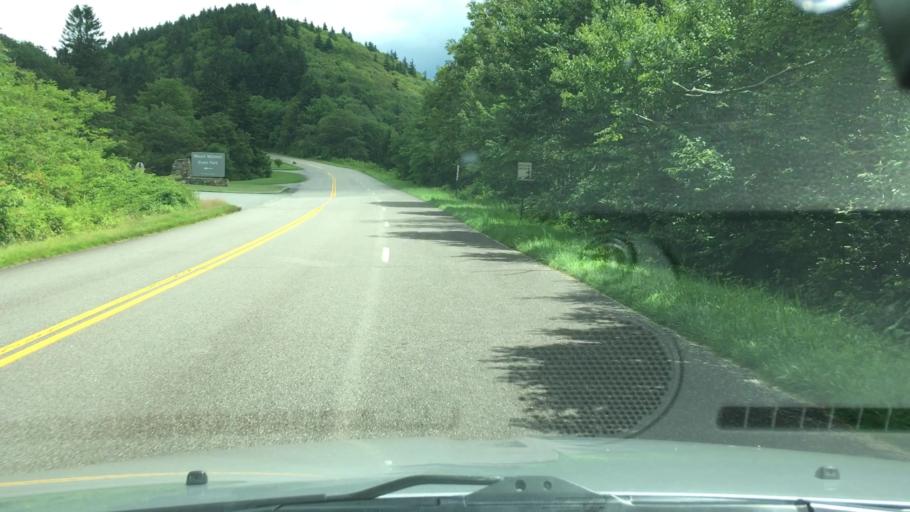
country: US
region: North Carolina
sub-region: Buncombe County
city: Black Mountain
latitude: 35.7184
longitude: -82.2801
